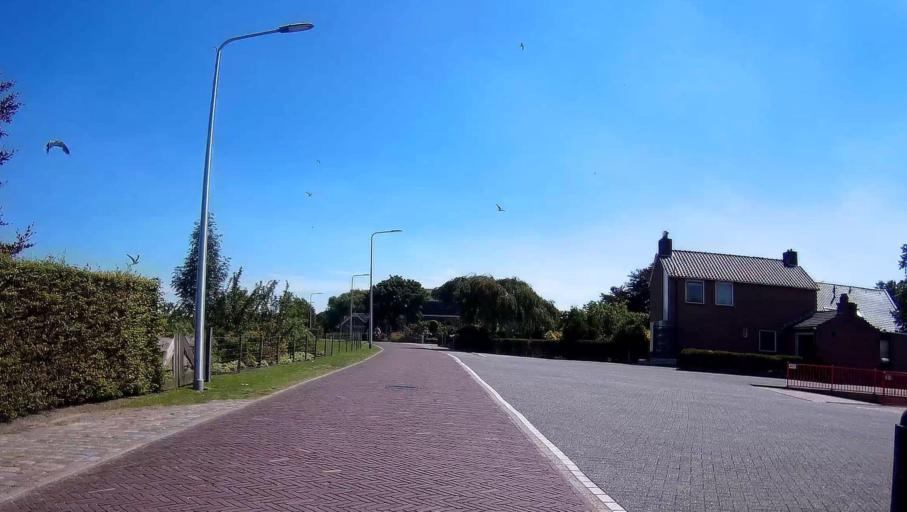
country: NL
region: South Holland
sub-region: Gemeente Westland
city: Naaldwijk
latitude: 52.0007
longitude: 4.1899
